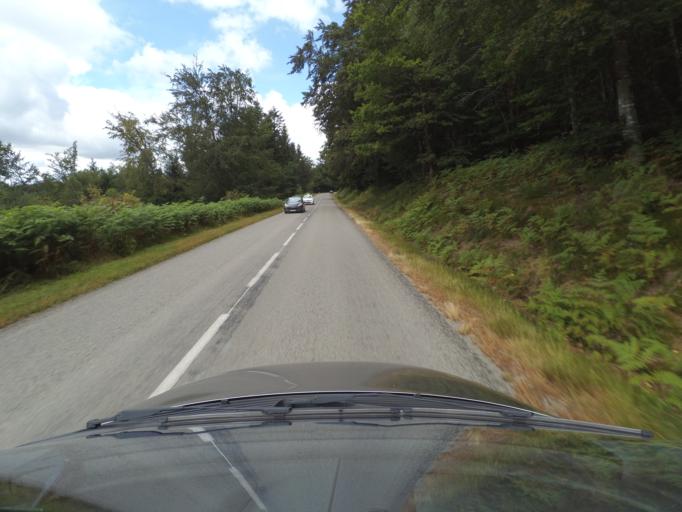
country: FR
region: Limousin
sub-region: Departement de la Creuse
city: Bourganeuf
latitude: 45.9060
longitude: 1.8587
